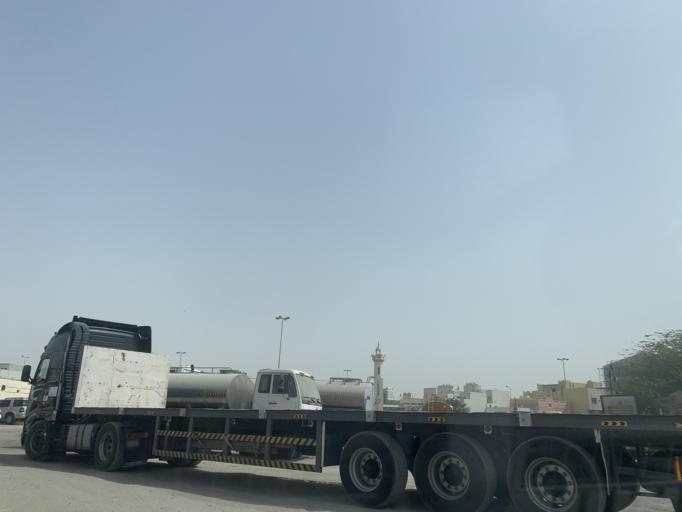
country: BH
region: Northern
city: Madinat `Isa
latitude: 26.1867
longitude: 50.5262
